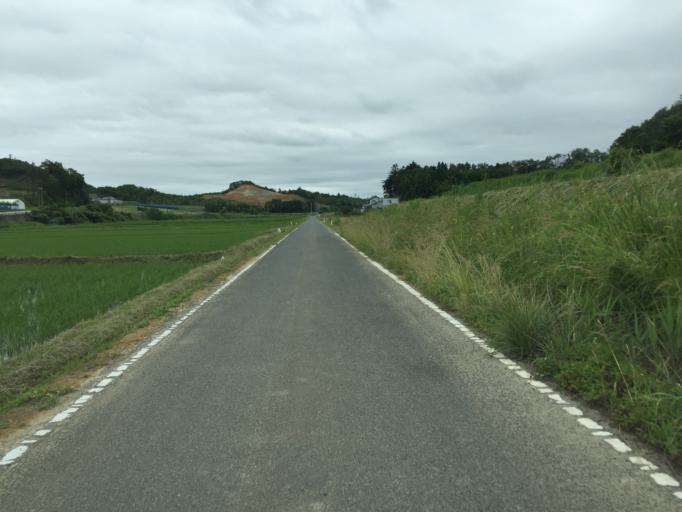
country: JP
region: Fukushima
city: Namie
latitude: 37.7510
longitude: 140.9939
